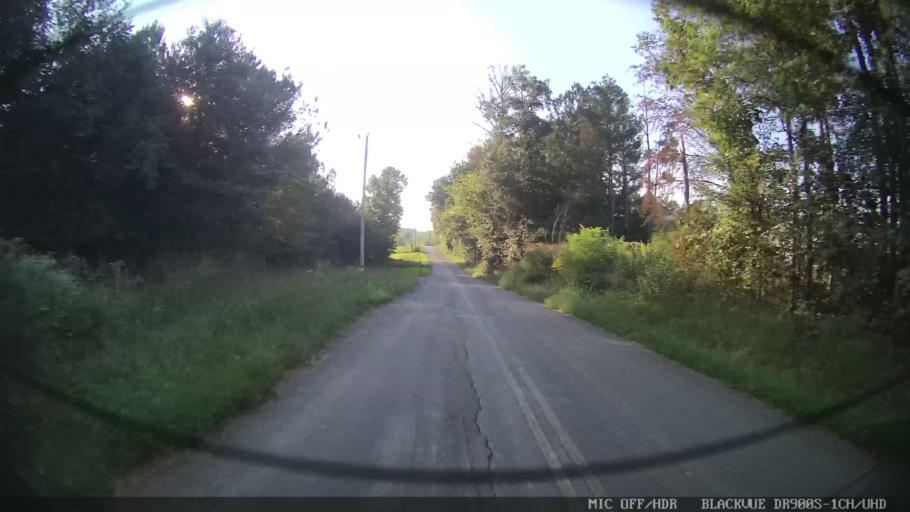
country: US
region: Tennessee
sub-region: Bradley County
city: Wildwood Lake
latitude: 35.0217
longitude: -84.7674
